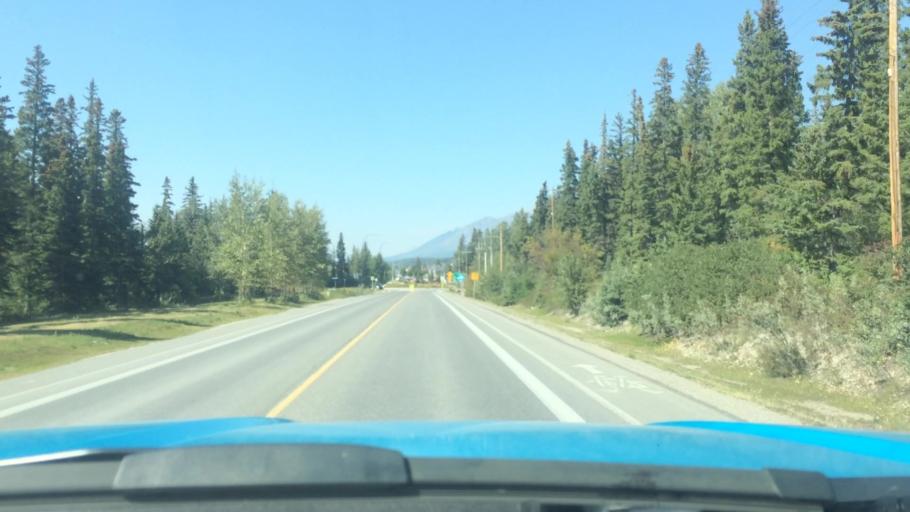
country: CA
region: Alberta
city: Canmore
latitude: 51.0831
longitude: -115.3431
